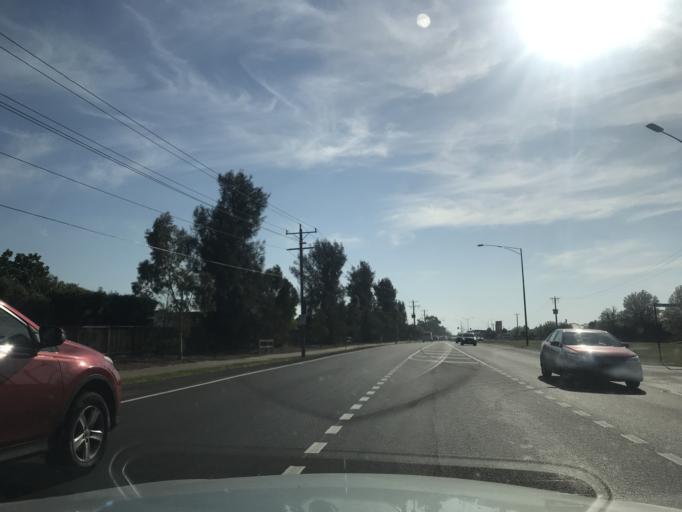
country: AU
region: Victoria
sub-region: Wyndham
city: Hoppers Crossing
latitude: -37.8509
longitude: 144.7102
